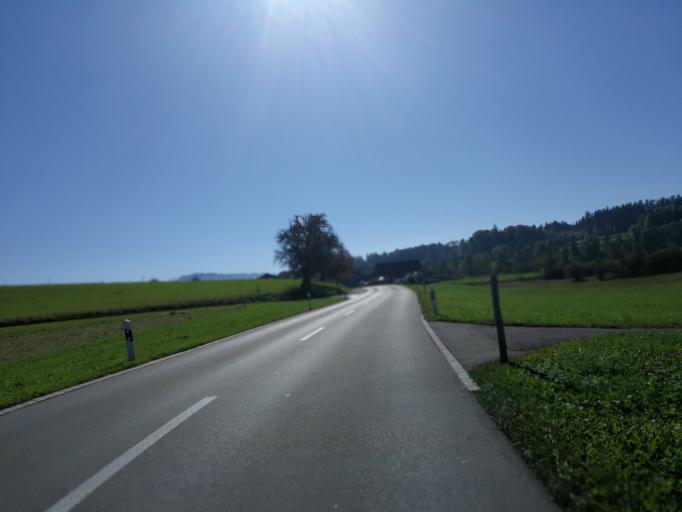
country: CH
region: Zurich
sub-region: Bezirk Hinwil
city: Binzikon
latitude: 47.2668
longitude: 8.7627
